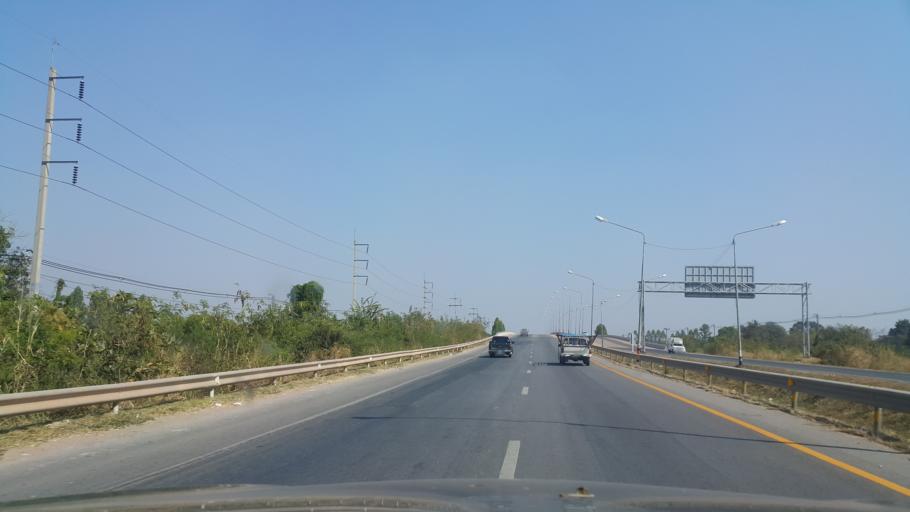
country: TH
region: Khon Kaen
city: Khon Kaen
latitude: 16.5117
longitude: 102.8411
